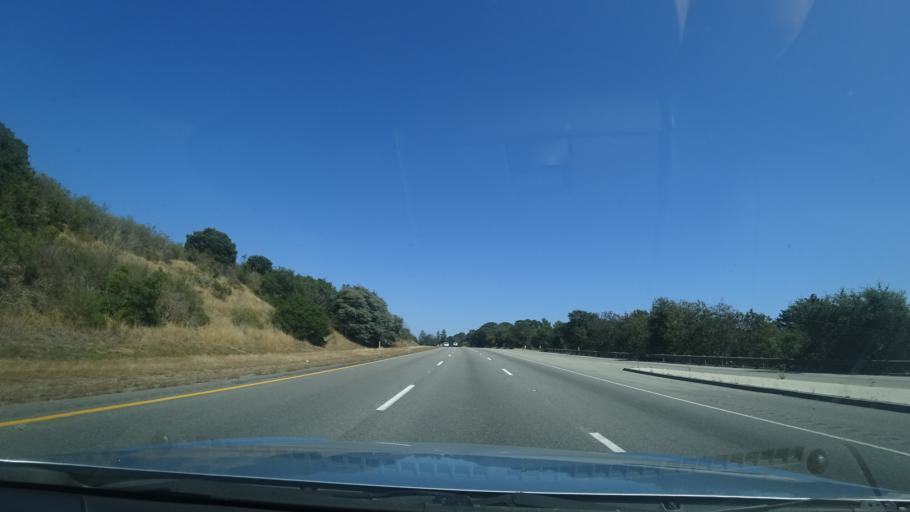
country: US
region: California
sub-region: Santa Cruz County
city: Aptos Hills-Larkin Valley
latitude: 36.9404
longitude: -121.8382
